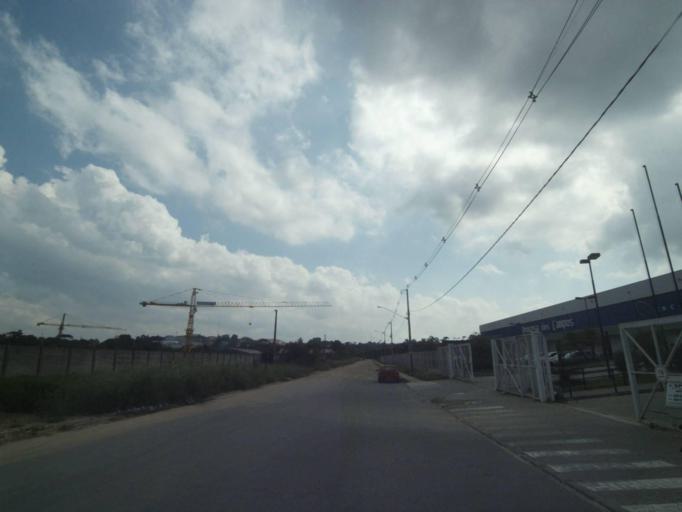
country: BR
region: Parana
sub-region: Araucaria
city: Araucaria
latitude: -25.5117
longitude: -49.3406
